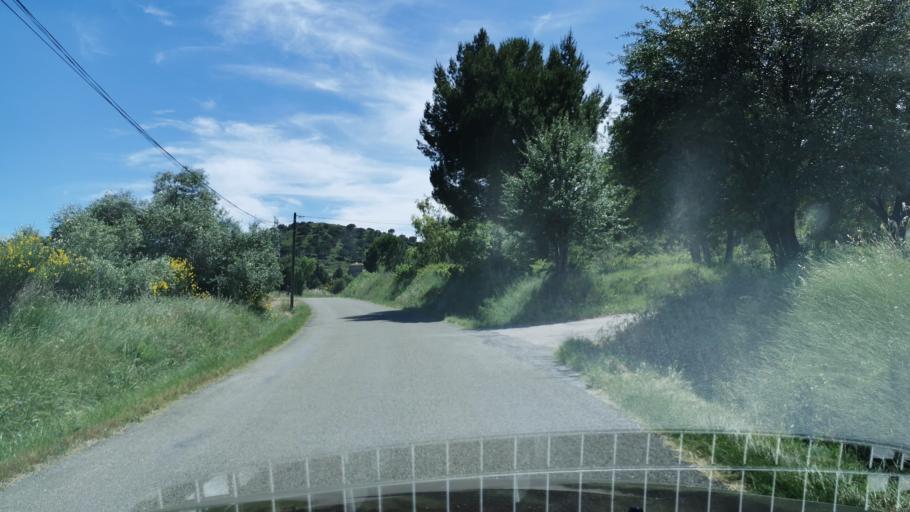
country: FR
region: Languedoc-Roussillon
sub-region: Departement de l'Aude
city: Nevian
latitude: 43.2049
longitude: 2.9033
